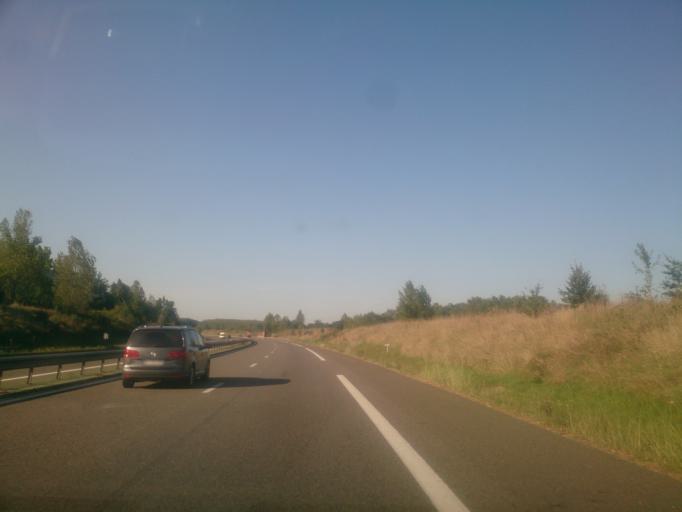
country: FR
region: Midi-Pyrenees
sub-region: Departement du Tarn-et-Garonne
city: Albias
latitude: 44.0617
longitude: 1.4225
